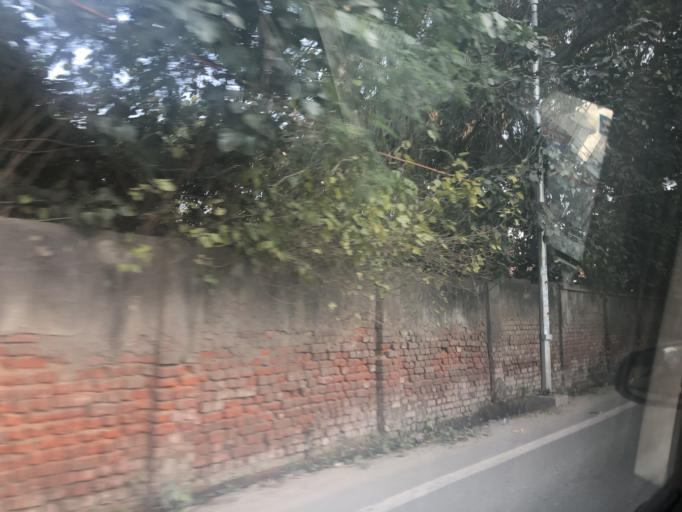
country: IN
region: Haryana
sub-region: Gurgaon
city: Gurgaon
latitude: 28.5630
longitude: 77.0013
